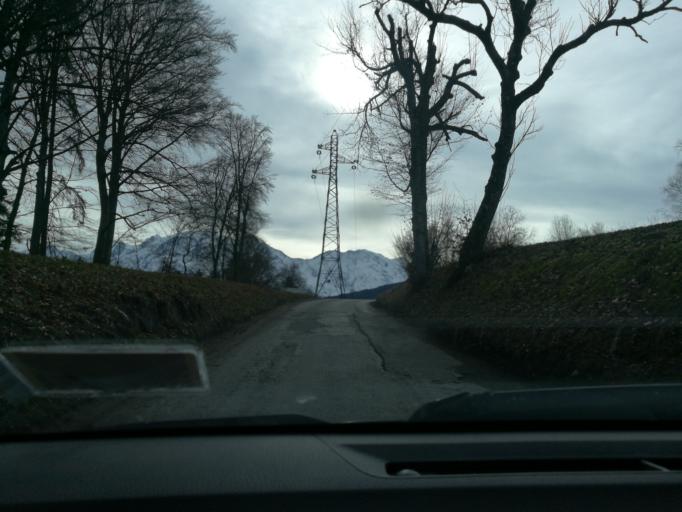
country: FR
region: Rhone-Alpes
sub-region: Departement de la Haute-Savoie
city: Domancy
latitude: 45.9151
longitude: 6.6307
